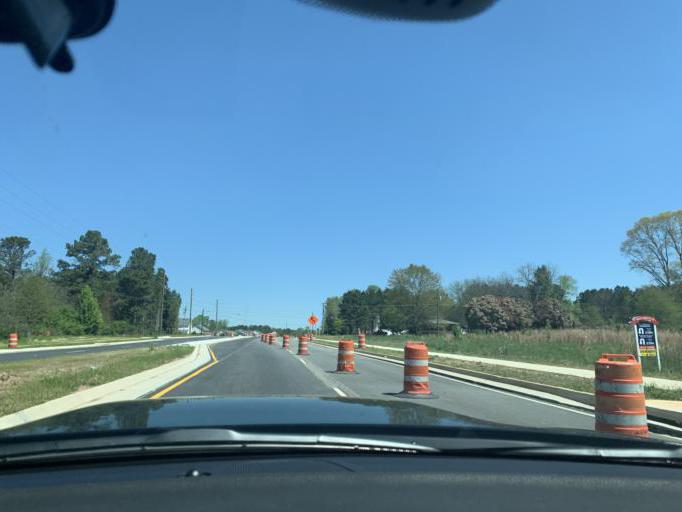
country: US
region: Georgia
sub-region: Forsyth County
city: Cumming
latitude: 34.2170
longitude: -84.1986
